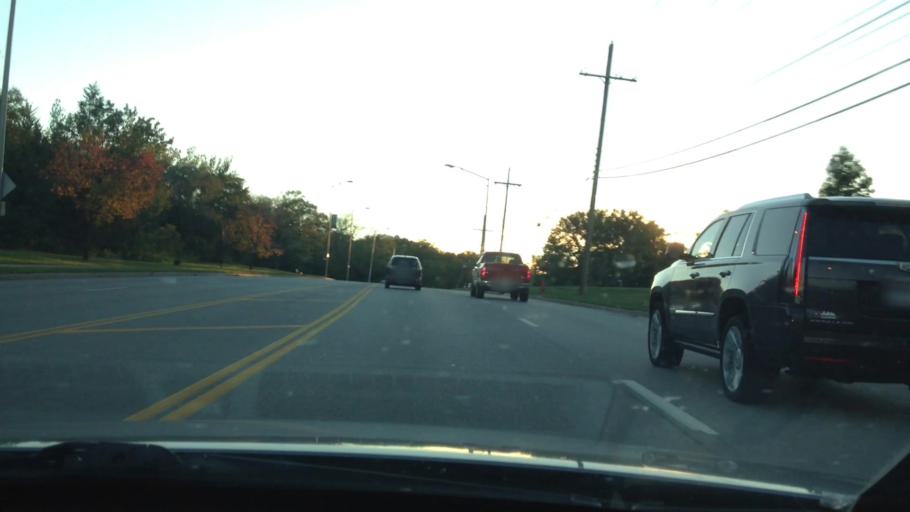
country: US
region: Missouri
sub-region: Jackson County
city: Raytown
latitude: 39.0132
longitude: -94.5292
